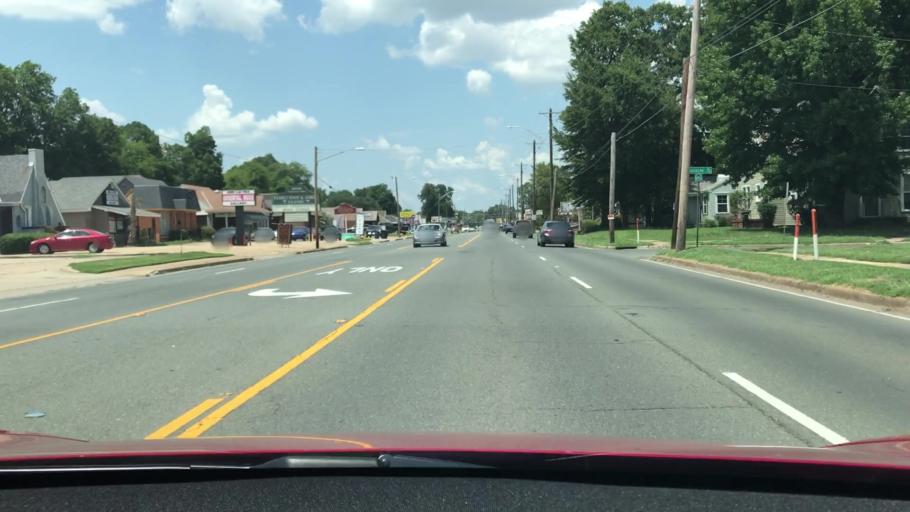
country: US
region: Louisiana
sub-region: Bossier Parish
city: Bossier City
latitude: 32.4726
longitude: -93.7221
